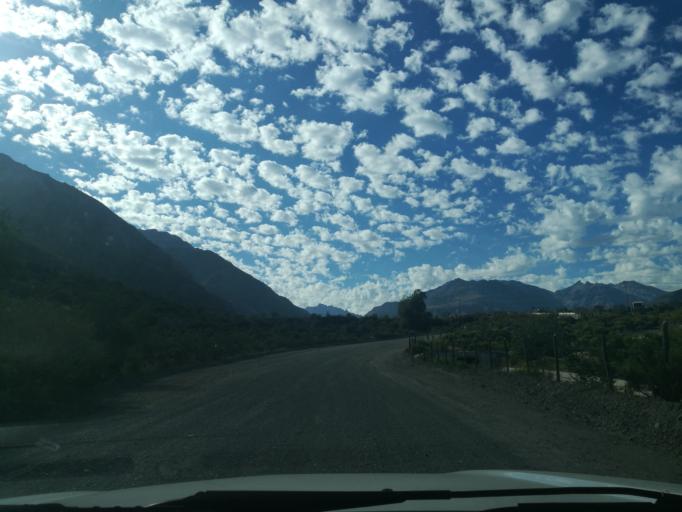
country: CL
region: O'Higgins
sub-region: Provincia de Cachapoal
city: Machali
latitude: -34.2928
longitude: -70.4337
